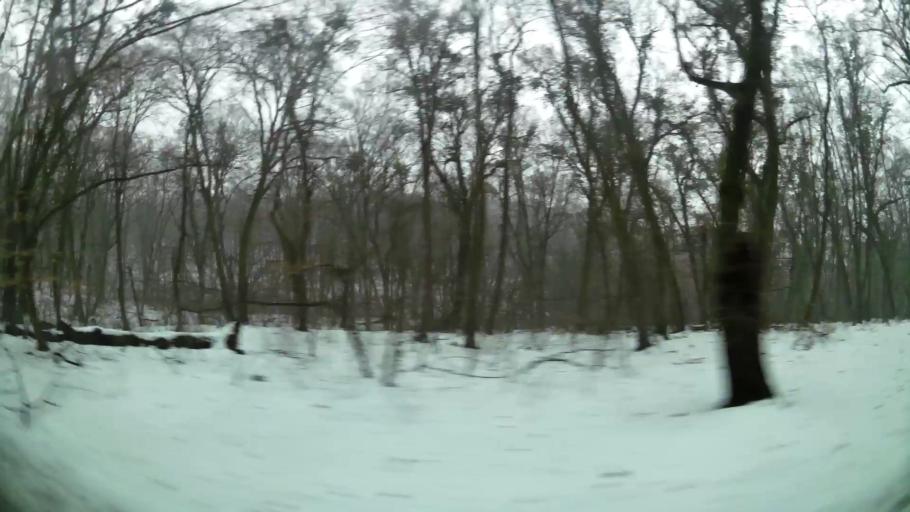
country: RS
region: Central Serbia
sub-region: Belgrade
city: Cukarica
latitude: 44.7746
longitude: 20.4317
